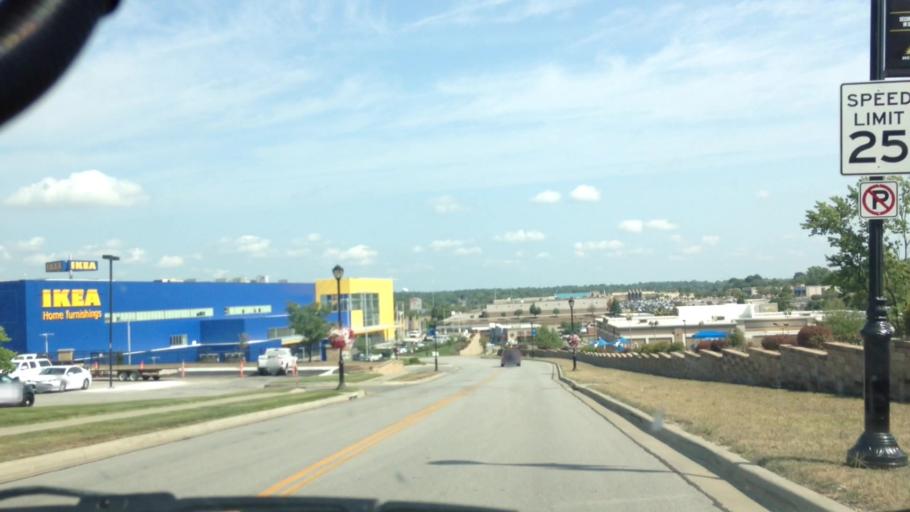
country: US
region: Kansas
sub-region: Johnson County
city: Merriam
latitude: 39.0175
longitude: -94.6896
